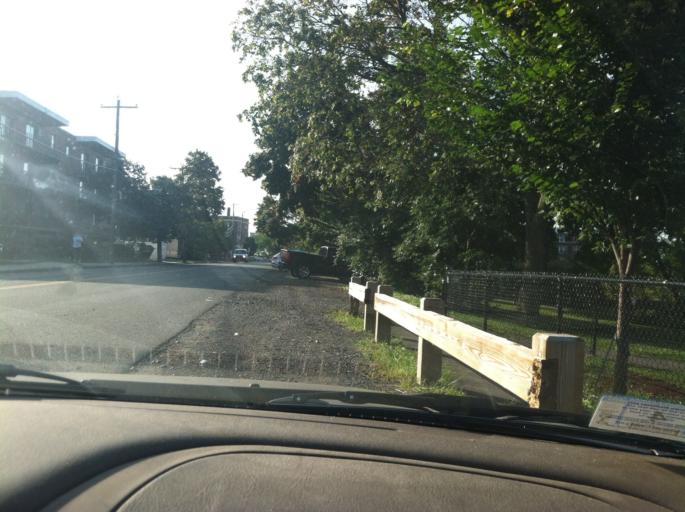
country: US
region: Massachusetts
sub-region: Suffolk County
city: Winthrop
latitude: 42.3745
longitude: -70.9724
